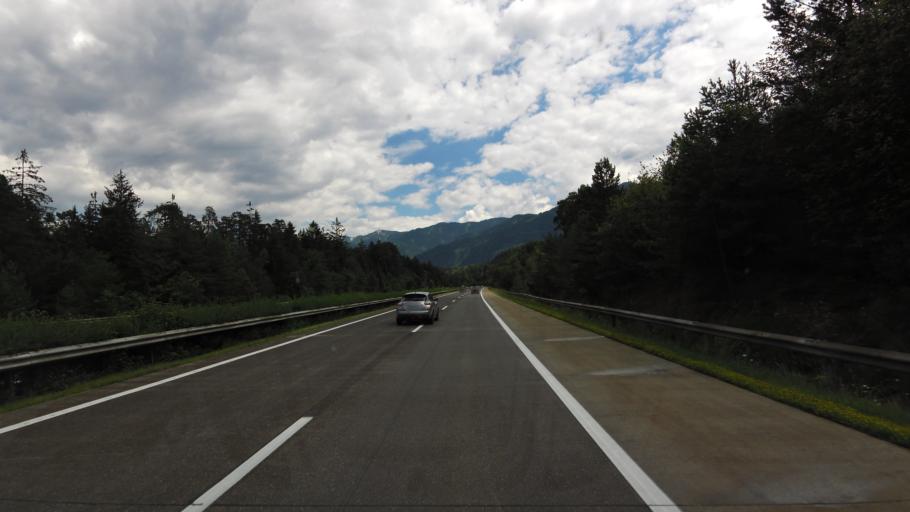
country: AT
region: Carinthia
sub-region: Politischer Bezirk Villach Land
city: Arnoldstein
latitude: 46.5638
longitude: 13.7397
